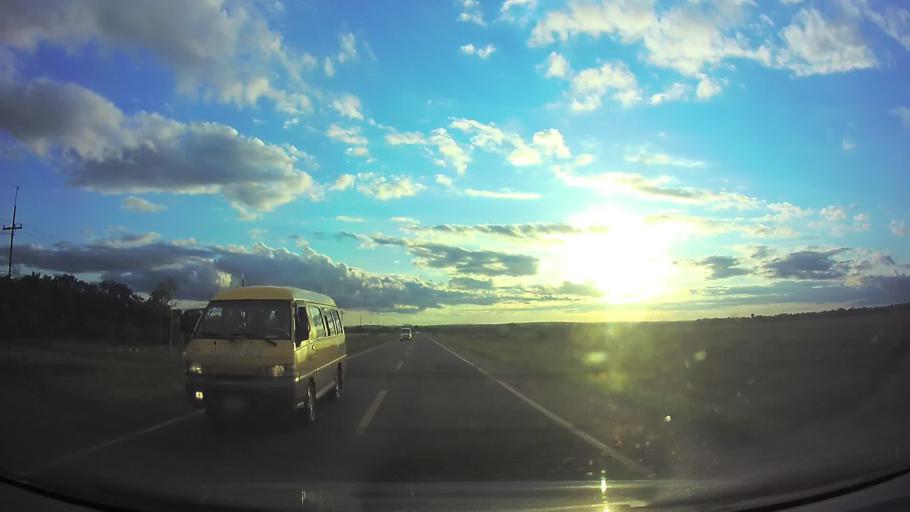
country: PY
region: Paraguari
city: Carapegua
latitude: -25.7162
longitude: -57.1960
